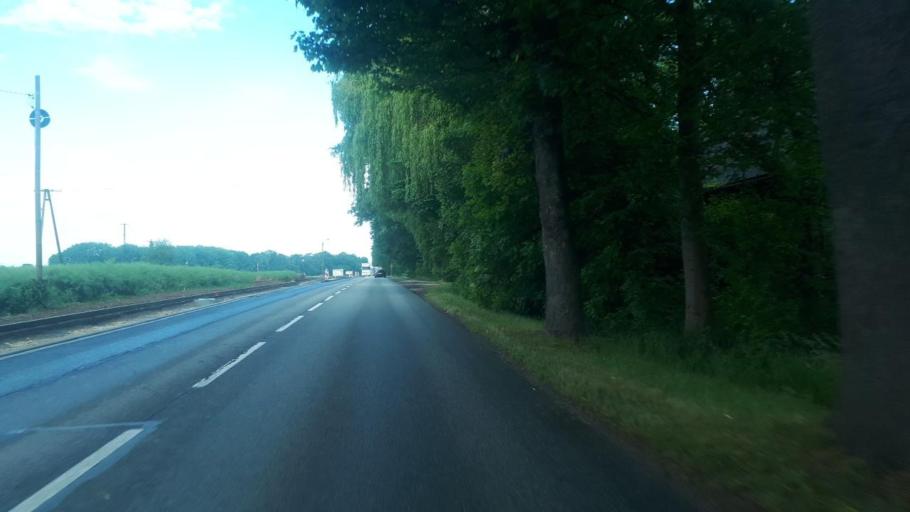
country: PL
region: Silesian Voivodeship
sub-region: Powiat pszczynski
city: Miedzna
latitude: 49.9704
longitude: 19.0226
